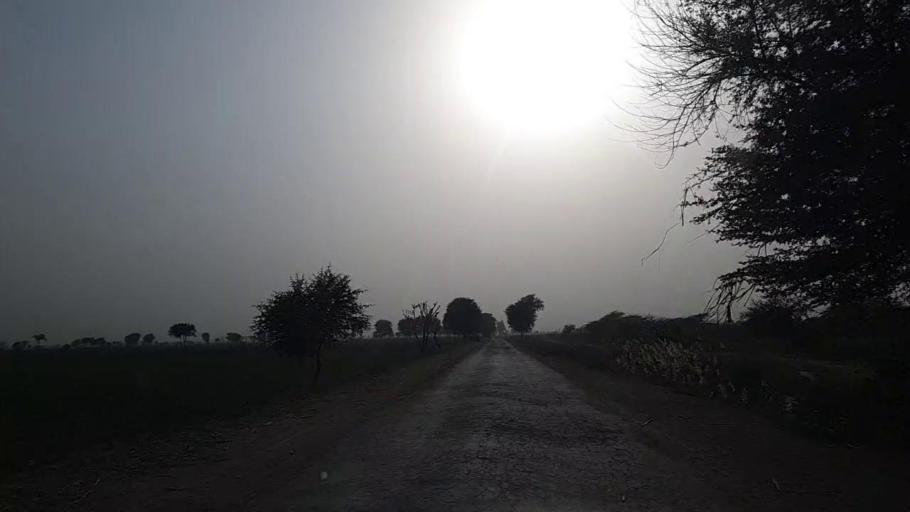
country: PK
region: Sindh
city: Pithoro
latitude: 25.4411
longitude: 69.2934
